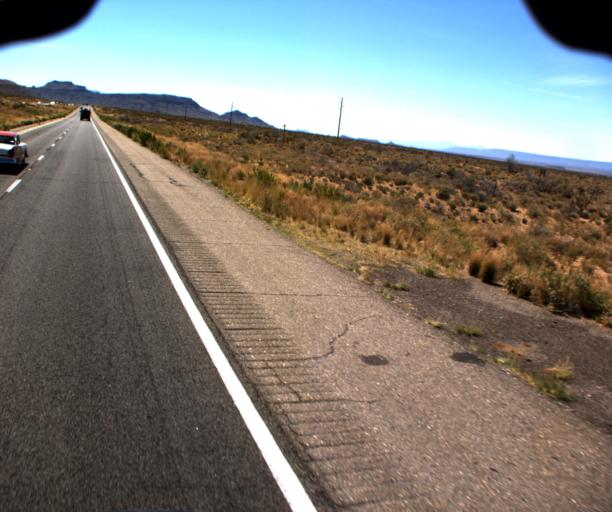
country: US
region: Arizona
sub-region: Mohave County
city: Golden Valley
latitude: 35.2637
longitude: -114.1631
